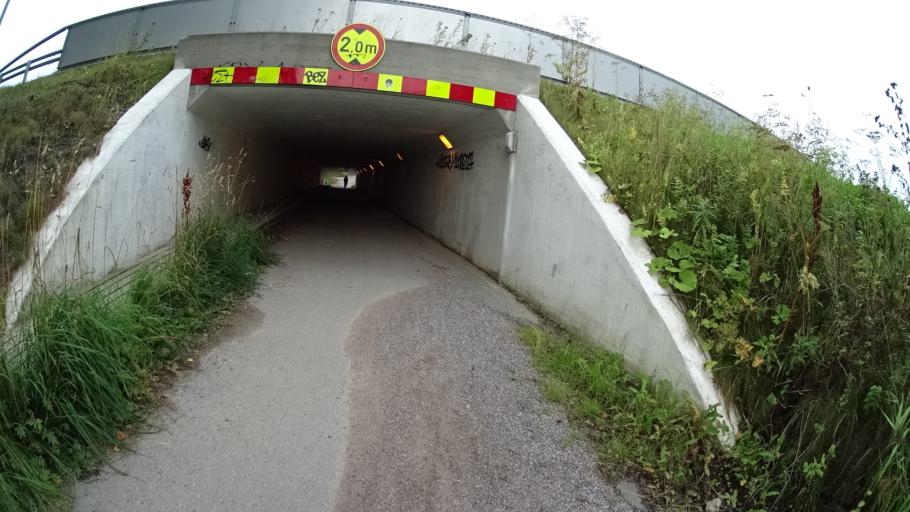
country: FI
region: Uusimaa
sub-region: Helsinki
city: Helsinki
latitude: 60.2190
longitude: 24.9785
